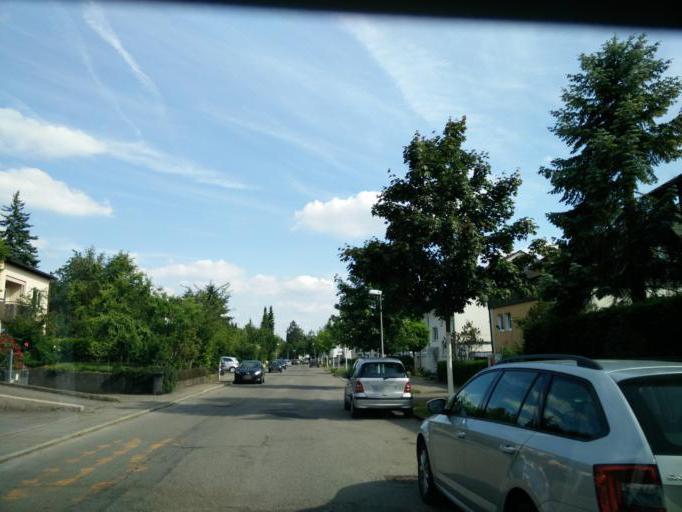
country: DE
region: Baden-Wuerttemberg
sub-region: Tuebingen Region
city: Tuebingen
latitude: 48.5374
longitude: 9.0503
